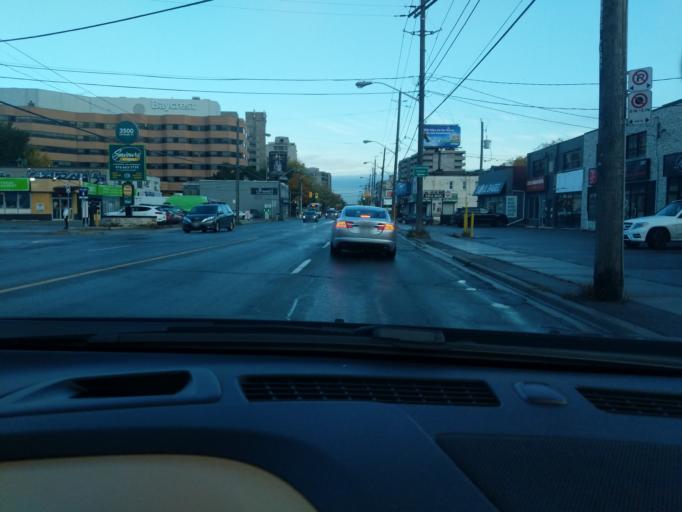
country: CA
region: Ontario
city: Toronto
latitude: 43.7285
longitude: -79.4318
